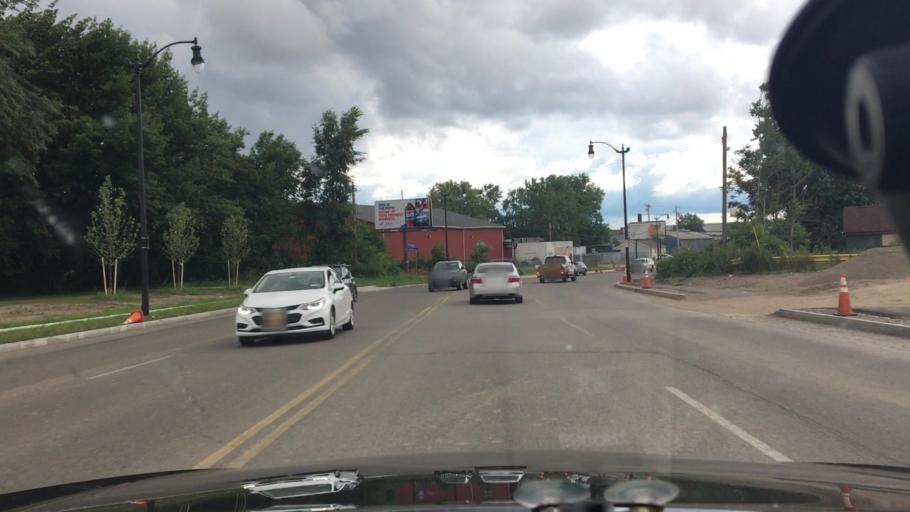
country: US
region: New York
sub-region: Erie County
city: West Seneca
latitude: 42.8629
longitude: -78.8257
